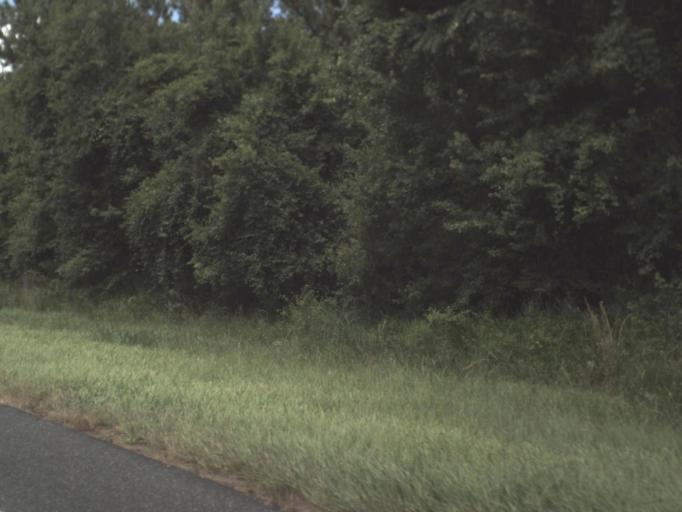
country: US
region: Florida
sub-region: Taylor County
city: Perry
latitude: 30.1865
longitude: -83.6426
